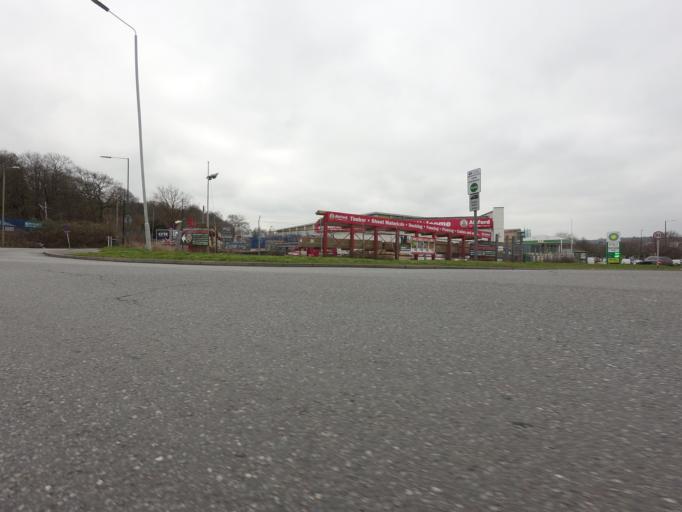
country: GB
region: England
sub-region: Greater London
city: Sidcup
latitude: 51.4150
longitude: 0.1263
